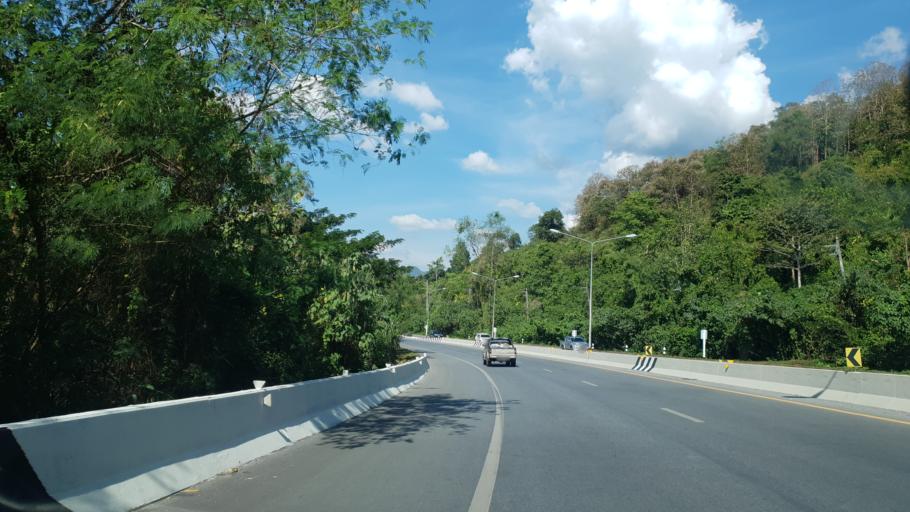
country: TH
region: Uttaradit
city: Lap Lae
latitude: 17.7846
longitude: 100.1183
